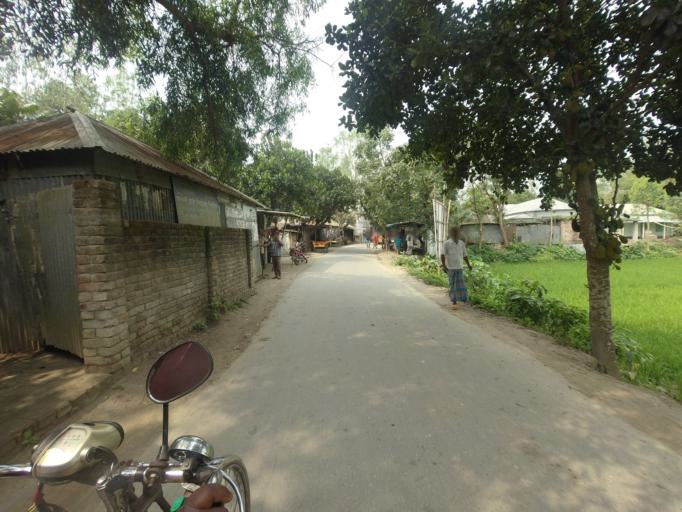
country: BD
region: Rajshahi
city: Sirajganj
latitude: 24.3511
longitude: 89.6755
